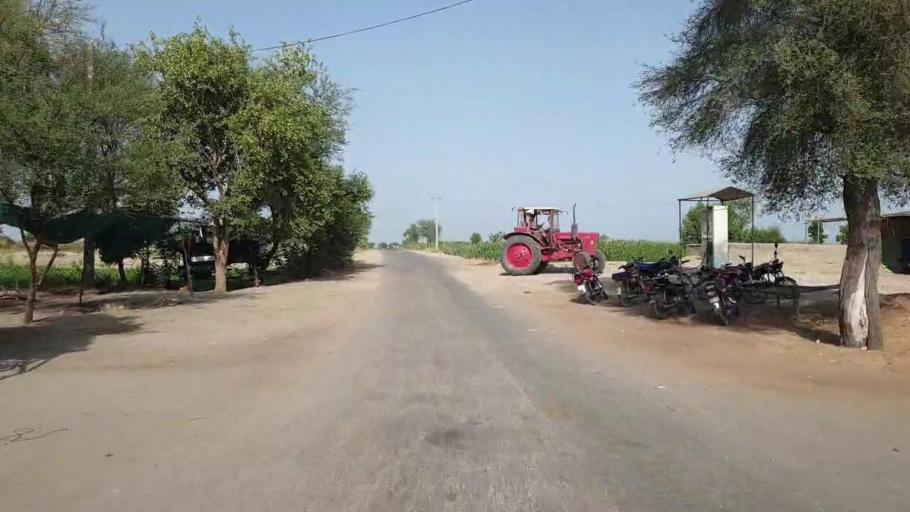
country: PK
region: Sindh
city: Sakrand
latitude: 26.2843
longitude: 68.2546
